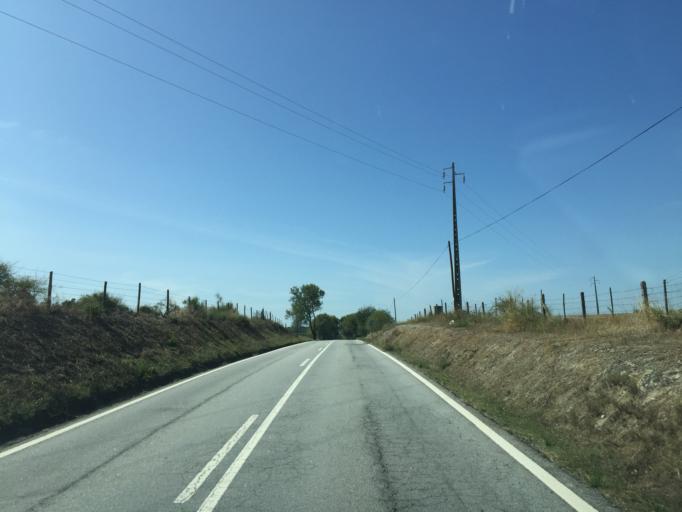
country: PT
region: Portalegre
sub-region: Portalegre
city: Alagoa
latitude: 39.4337
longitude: -7.5779
